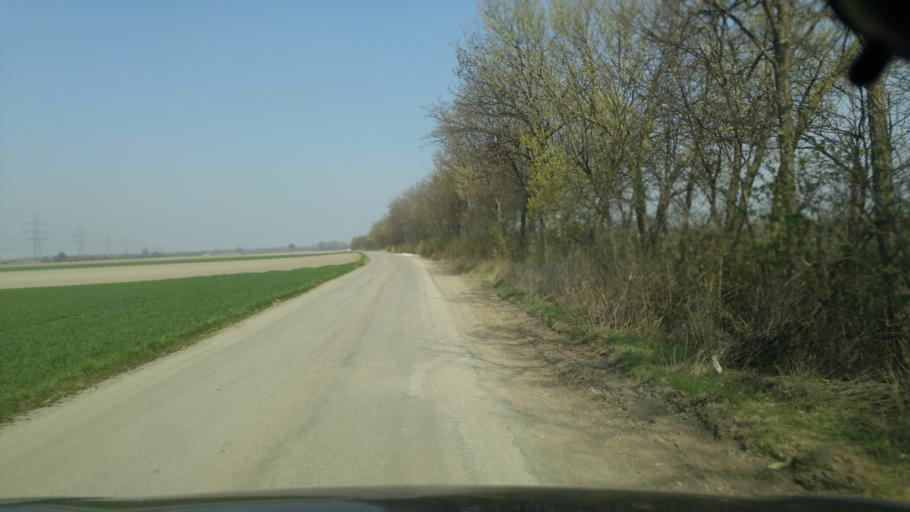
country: AT
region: Lower Austria
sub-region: Politischer Bezirk Modling
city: Munchendorf
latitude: 48.0280
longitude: 16.3930
